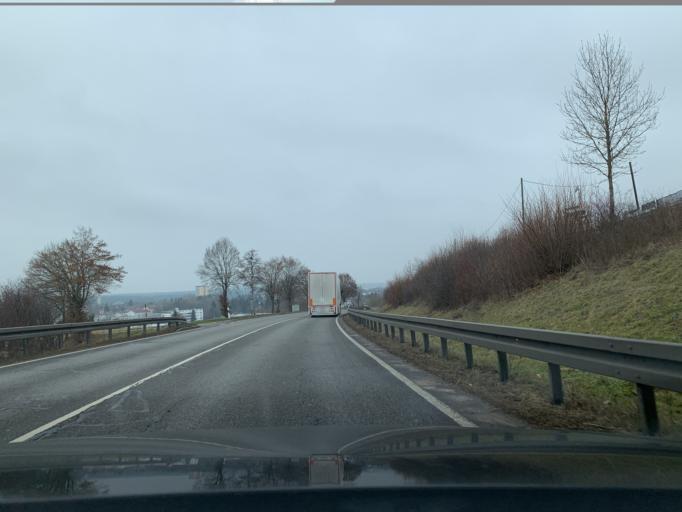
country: DE
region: Baden-Wuerttemberg
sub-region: Freiburg Region
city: Villingen-Schwenningen
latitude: 48.0687
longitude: 8.4641
